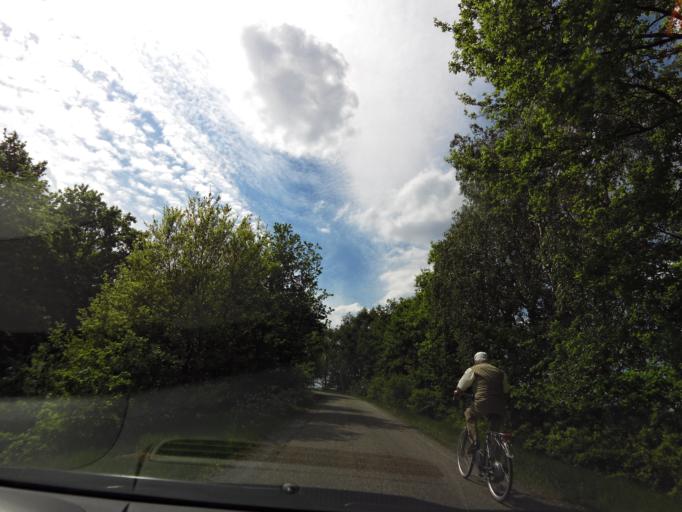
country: NL
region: Limburg
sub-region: Gemeente Peel en Maas
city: Maasbree
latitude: 51.3786
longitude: 5.9600
